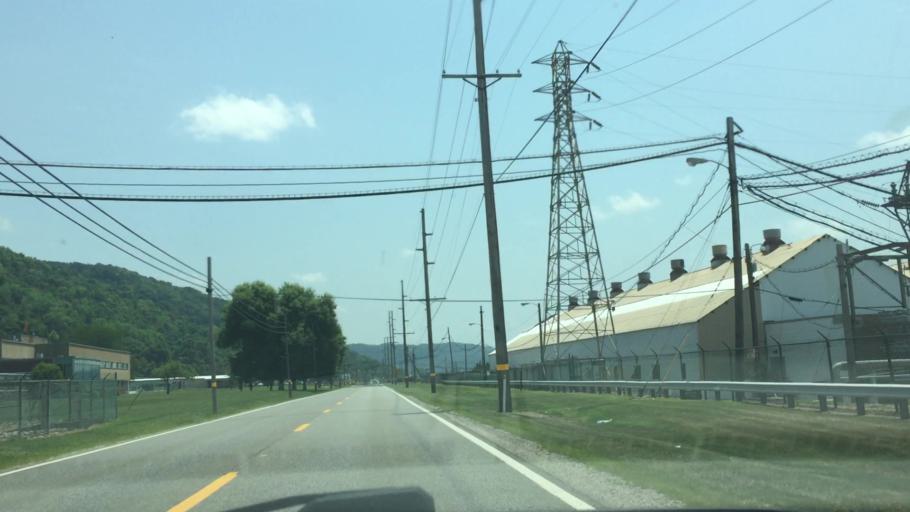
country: US
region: West Virginia
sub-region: Wetzel County
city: New Martinsville
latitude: 39.7502
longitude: -80.8519
